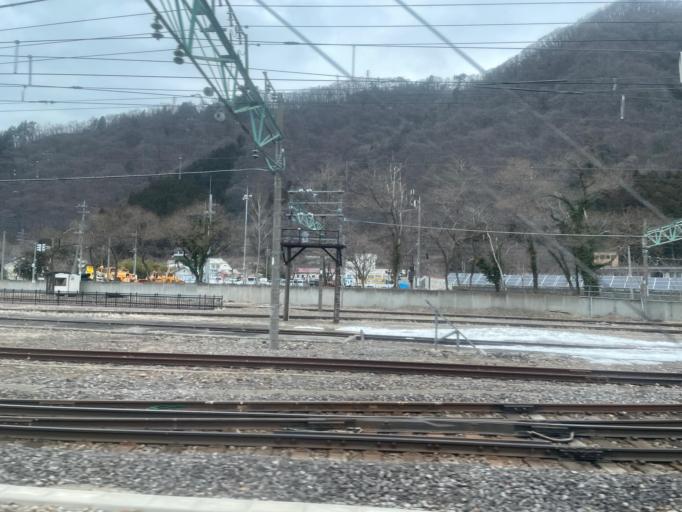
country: JP
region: Gunma
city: Numata
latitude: 36.7814
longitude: 138.9704
